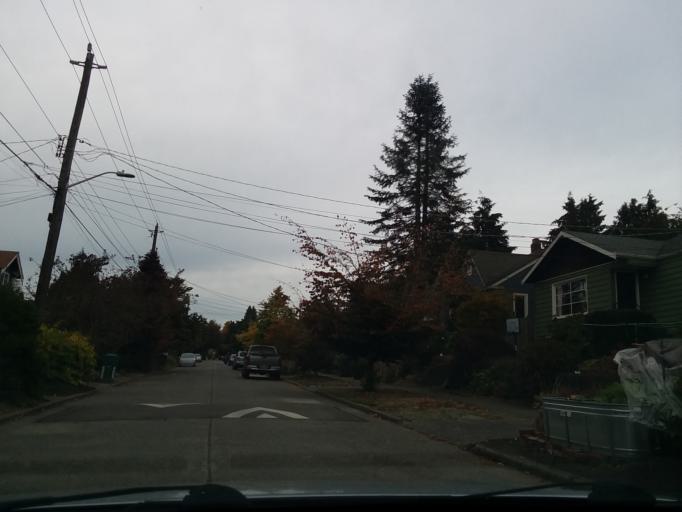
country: US
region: Washington
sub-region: King County
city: Shoreline
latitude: 47.6800
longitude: -122.3789
